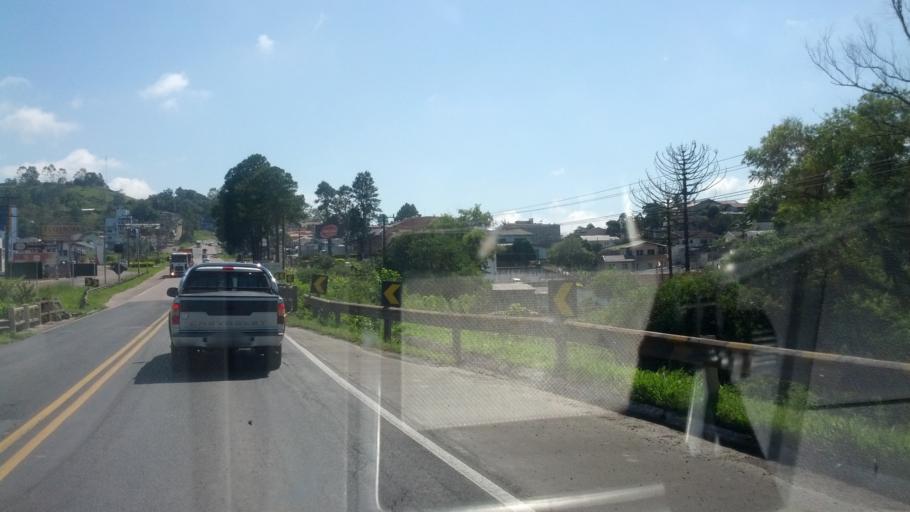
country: BR
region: Santa Catarina
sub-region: Rio Do Sul
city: Rio do Sul
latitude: -27.2085
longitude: -49.6507
